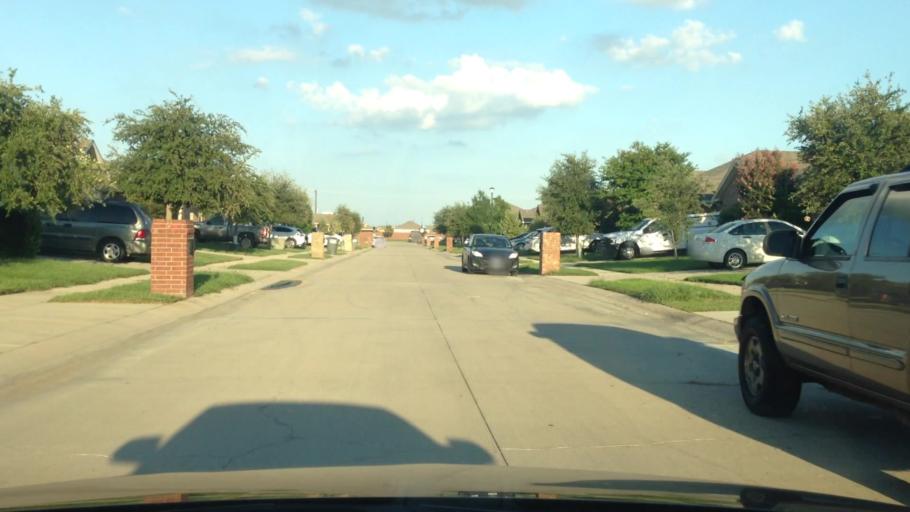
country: US
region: Texas
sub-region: Denton County
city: Little Elm
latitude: 33.1436
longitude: -96.9166
